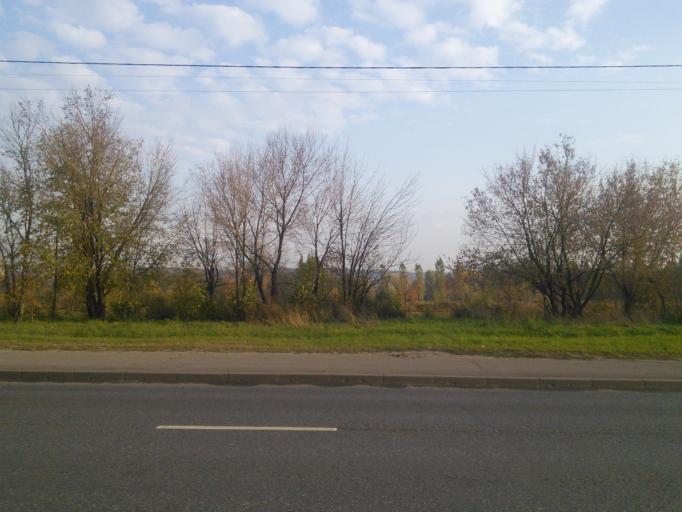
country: RU
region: Moskovskaya
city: Fili
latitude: 55.7568
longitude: 37.4626
